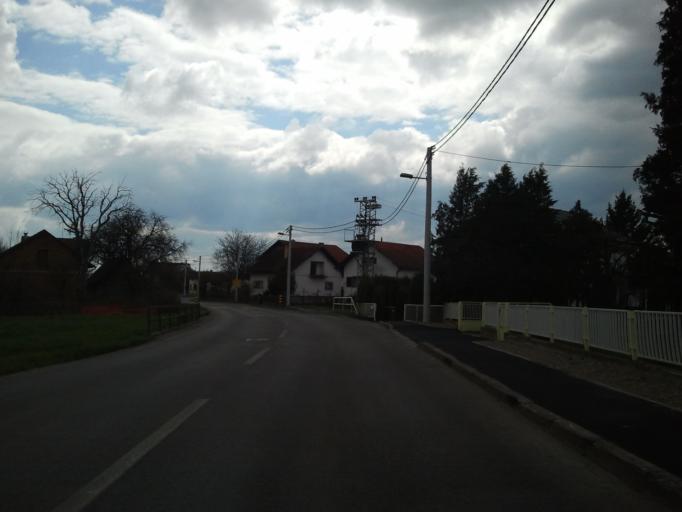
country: HR
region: Grad Zagreb
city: Zadvorsko
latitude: 45.7171
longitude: 15.9403
